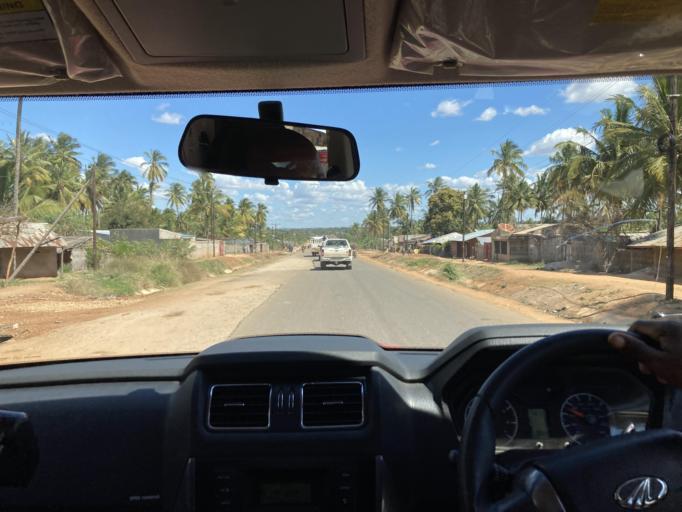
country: MZ
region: Cabo Delgado
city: Montepuez
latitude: -13.1326
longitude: 38.9930
